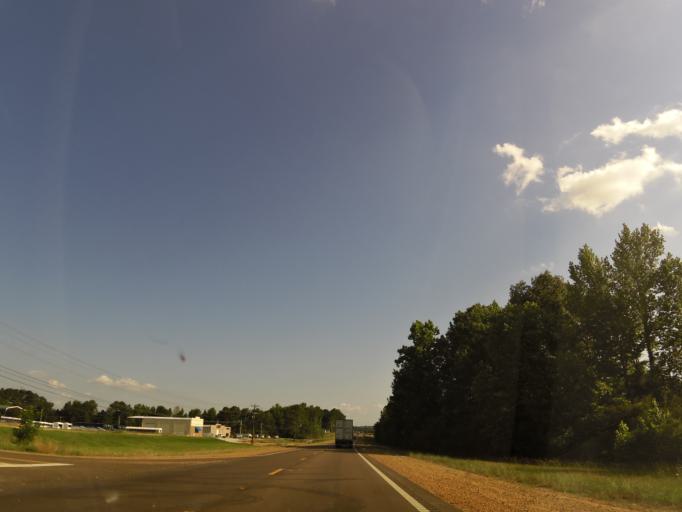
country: US
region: Mississippi
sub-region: Lafayette County
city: University
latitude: 34.2828
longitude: -89.5204
